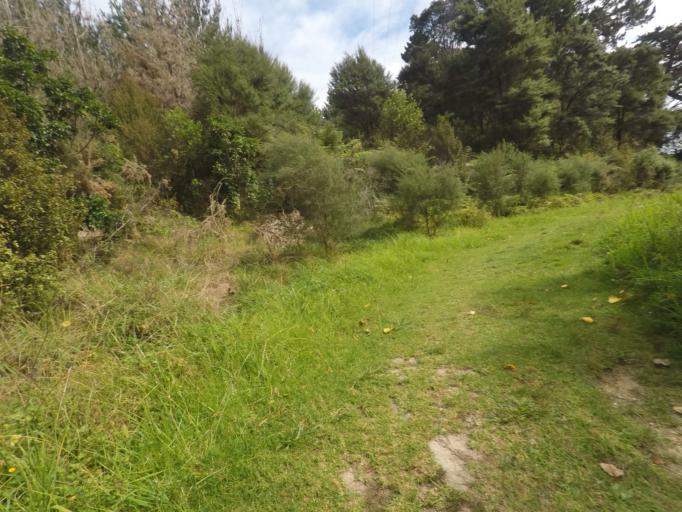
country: NZ
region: Auckland
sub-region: Auckland
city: Rothesay Bay
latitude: -36.6453
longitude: 174.7242
